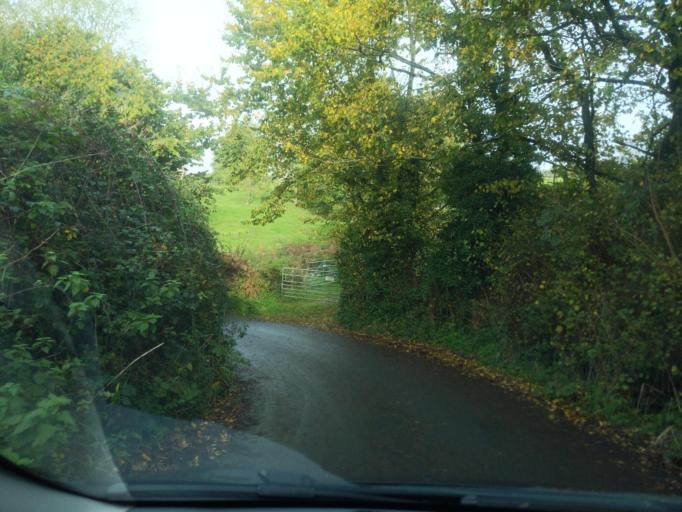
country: GB
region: England
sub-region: Cornwall
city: Looe
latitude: 50.3686
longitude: -4.4155
